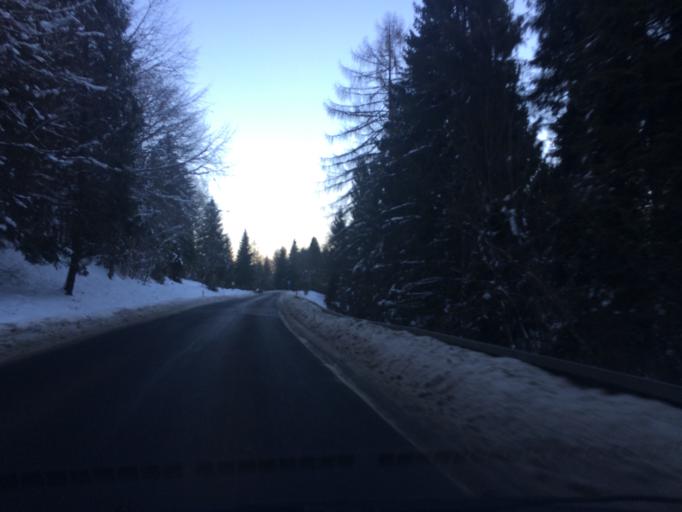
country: PL
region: Subcarpathian Voivodeship
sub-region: Powiat bieszczadzki
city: Lutowiska
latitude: 49.2836
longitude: 22.6826
